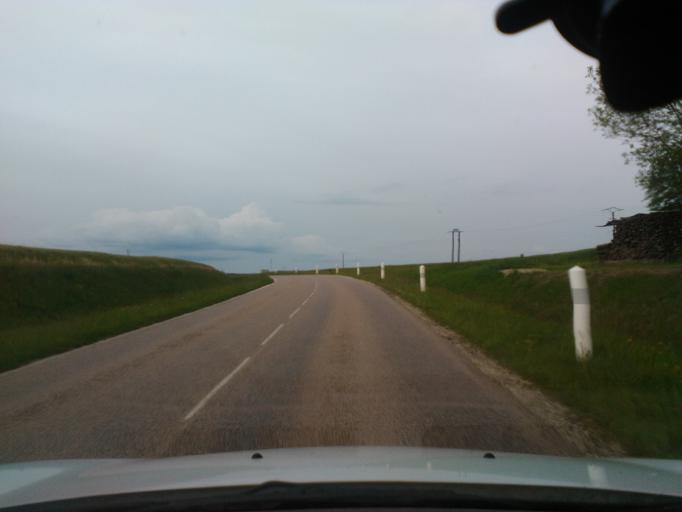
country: FR
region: Champagne-Ardenne
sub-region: Departement de la Haute-Marne
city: Doulaincourt-Saucourt
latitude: 48.2253
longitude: 5.2621
